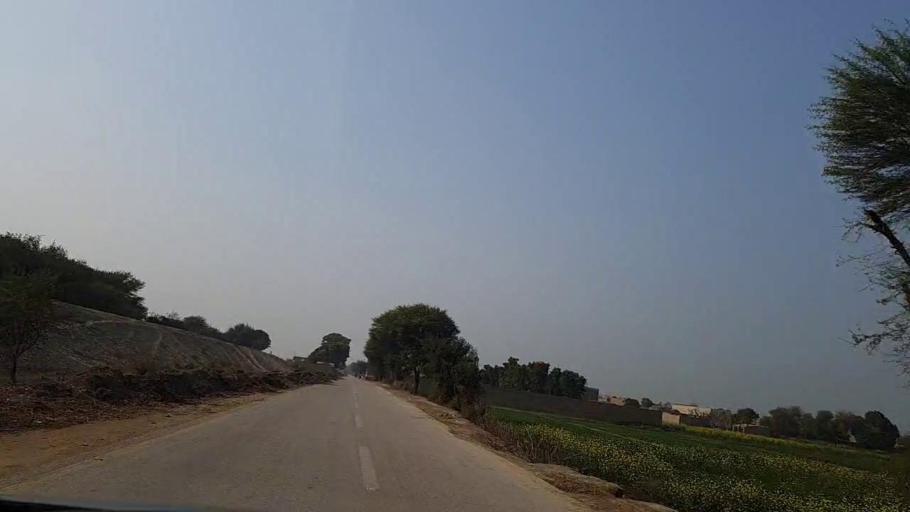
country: PK
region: Sindh
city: Sann
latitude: 26.1482
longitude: 68.1317
